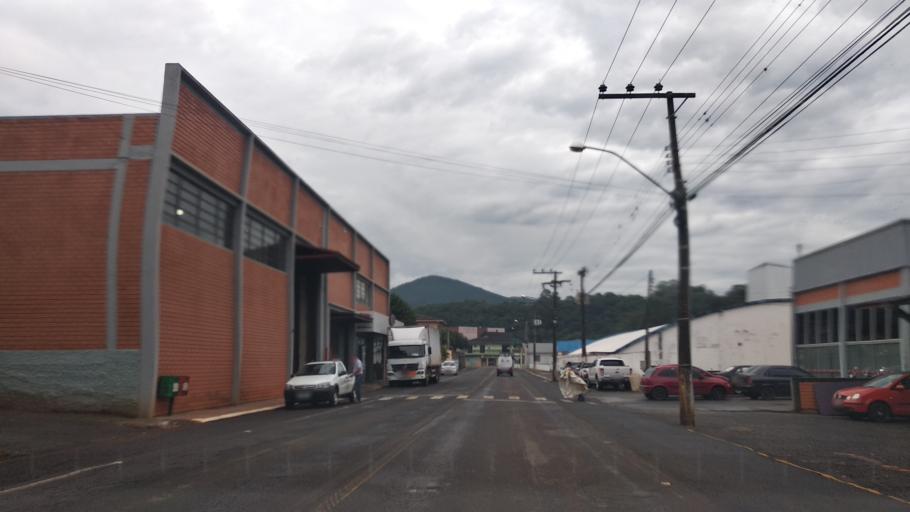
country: BR
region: Santa Catarina
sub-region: Videira
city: Videira
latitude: -27.1012
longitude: -51.2494
